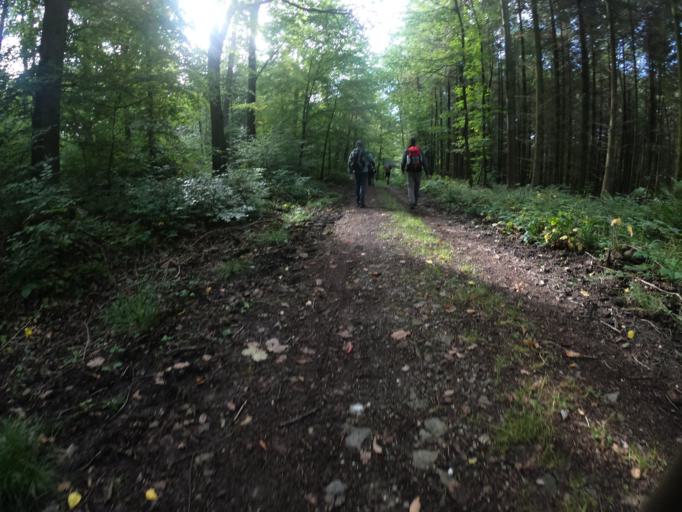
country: DE
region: Hesse
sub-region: Regierungsbezirk Darmstadt
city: Niedernhausen
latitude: 50.1294
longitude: 8.2756
